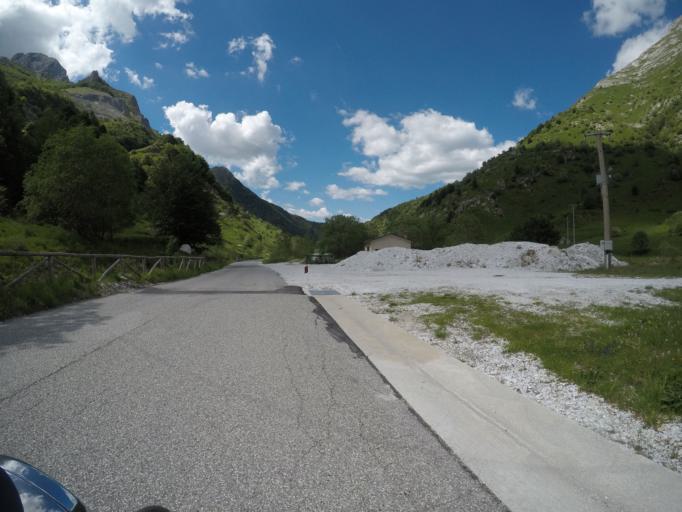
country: IT
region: Tuscany
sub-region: Provincia di Lucca
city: Minucciano
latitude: 44.1342
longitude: 10.1974
